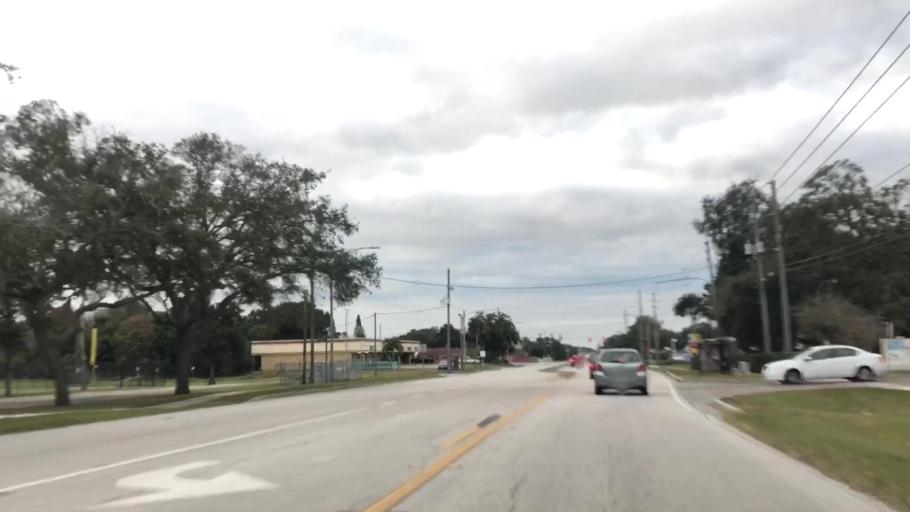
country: US
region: Florida
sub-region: Pinellas County
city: Dunedin
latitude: 27.9919
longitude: -82.7548
